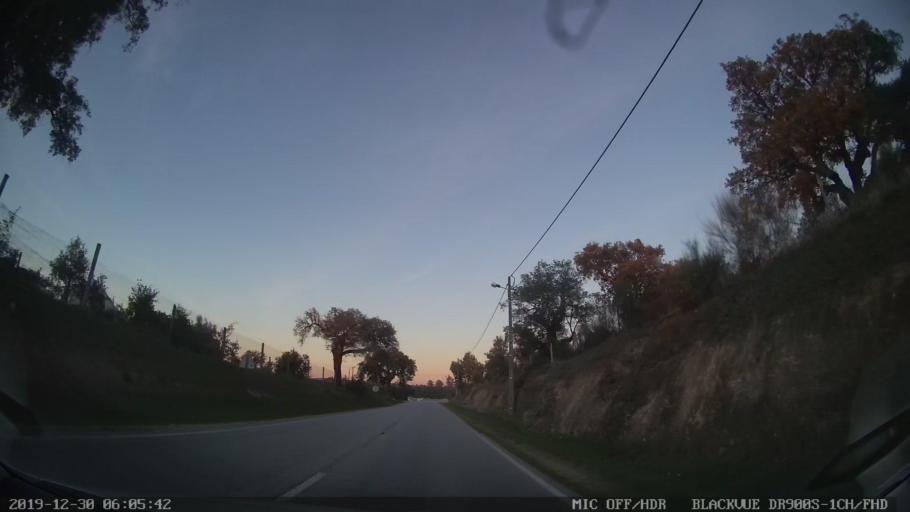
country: PT
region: Castelo Branco
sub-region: Penamacor
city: Penamacor
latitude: 40.0926
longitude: -7.2360
